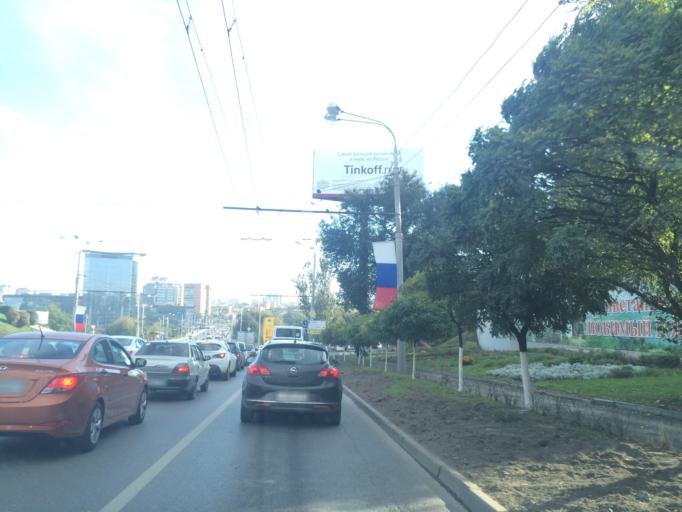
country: RU
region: Rostov
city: Rostov-na-Donu
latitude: 47.2125
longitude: 39.6927
